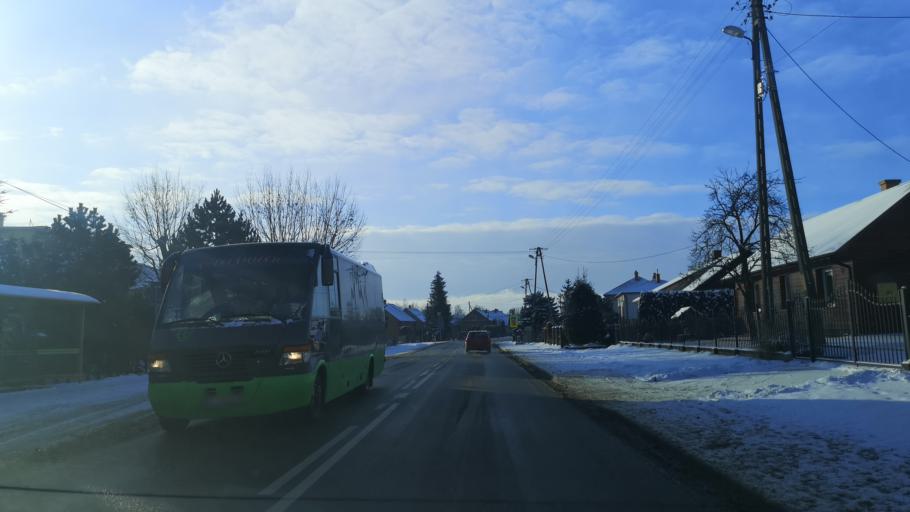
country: PL
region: Subcarpathian Voivodeship
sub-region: Powiat przeworski
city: Gorliczyna
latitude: 50.1054
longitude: 22.4974
